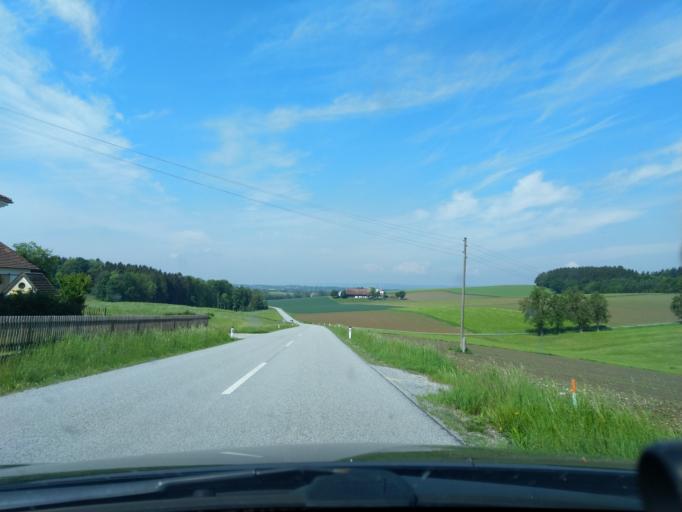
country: DE
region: Bavaria
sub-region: Lower Bavaria
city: Bad Fussing
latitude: 48.3025
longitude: 13.3876
